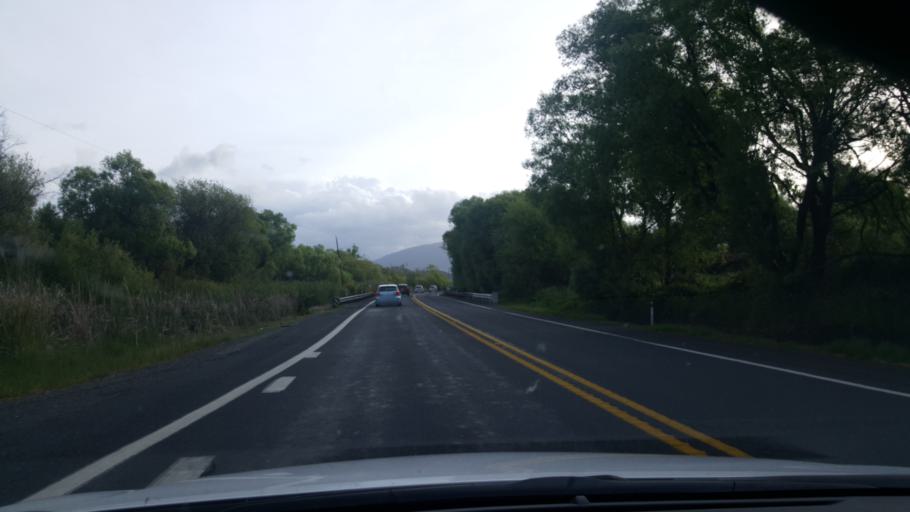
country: NZ
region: Waikato
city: Turangi
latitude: -38.9489
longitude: 175.8497
